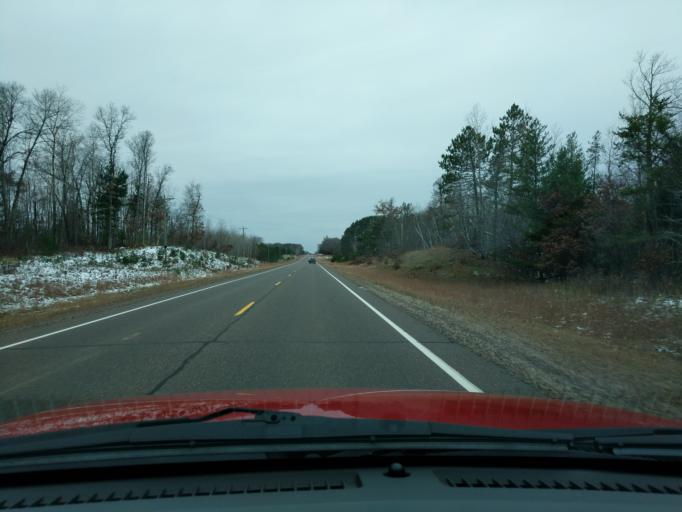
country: US
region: Wisconsin
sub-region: Burnett County
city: Siren
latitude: 45.8089
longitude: -92.1558
